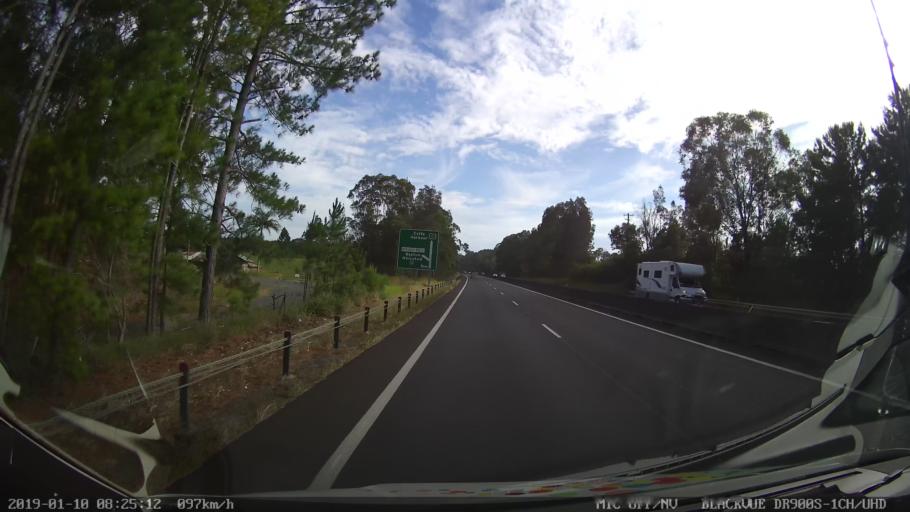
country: AU
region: New South Wales
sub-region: Coffs Harbour
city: Bonville
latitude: -30.4369
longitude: 153.0149
